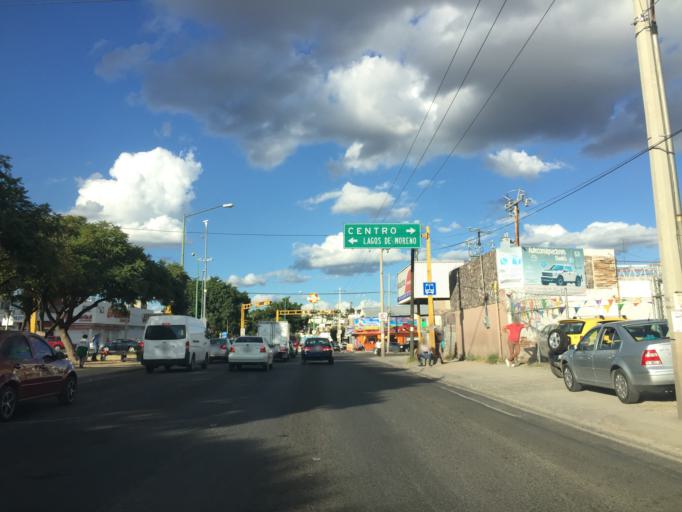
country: MX
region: Guanajuato
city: Leon
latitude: 21.1166
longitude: -101.7086
